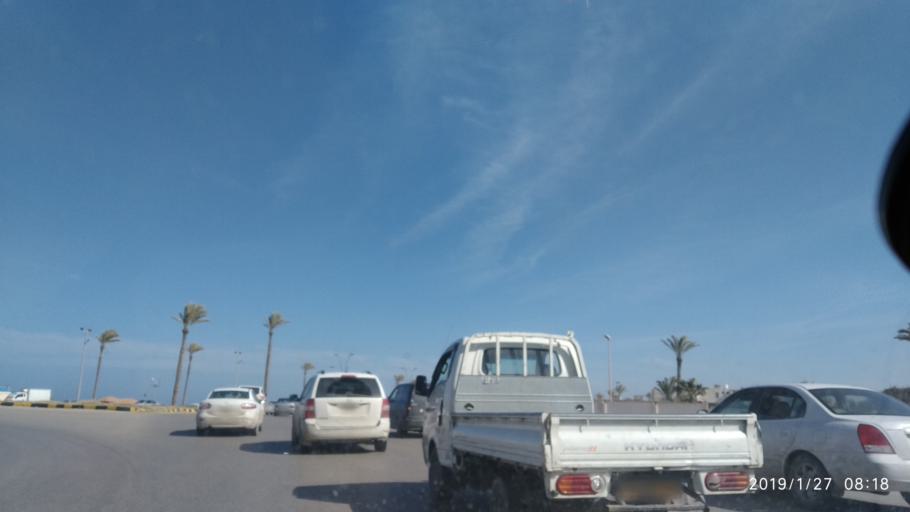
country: LY
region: Tripoli
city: Tripoli
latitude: 32.9068
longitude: 13.2678
